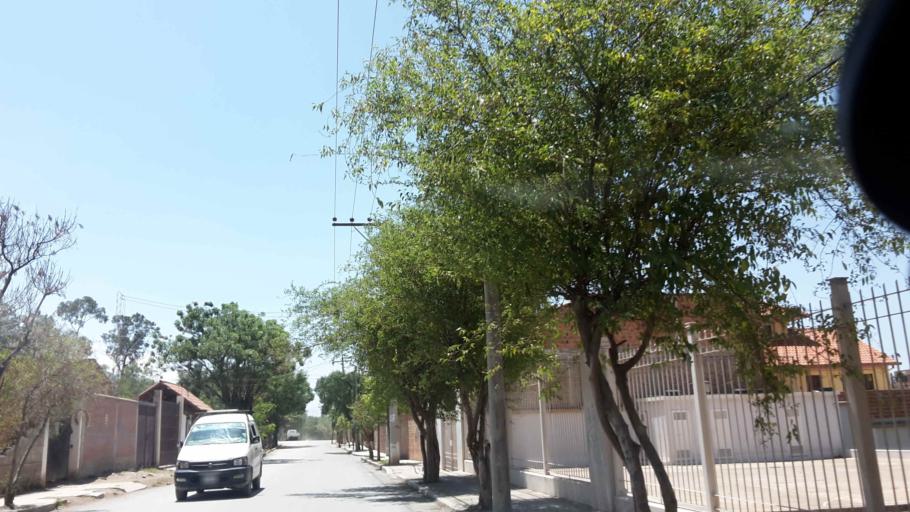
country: BO
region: Cochabamba
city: Cochabamba
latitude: -17.3370
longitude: -66.2158
